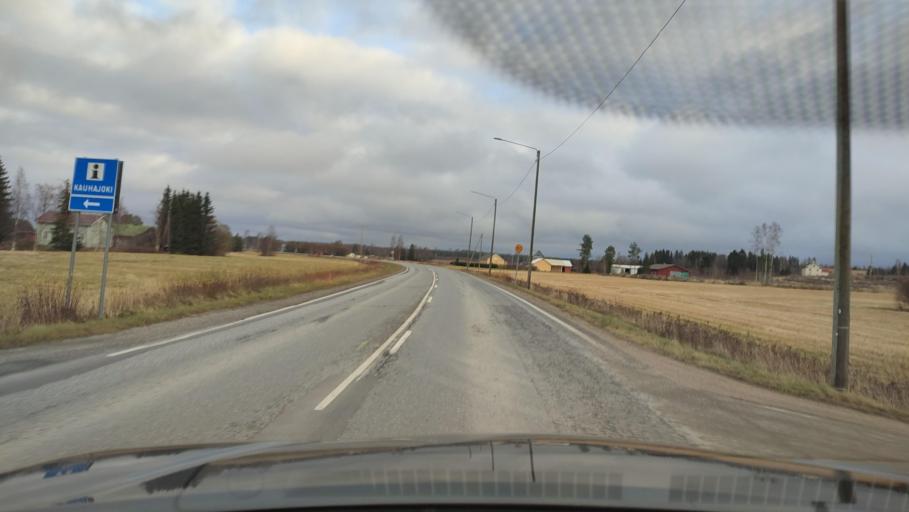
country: FI
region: Southern Ostrobothnia
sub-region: Suupohja
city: Kauhajoki
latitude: 62.3570
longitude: 22.0651
